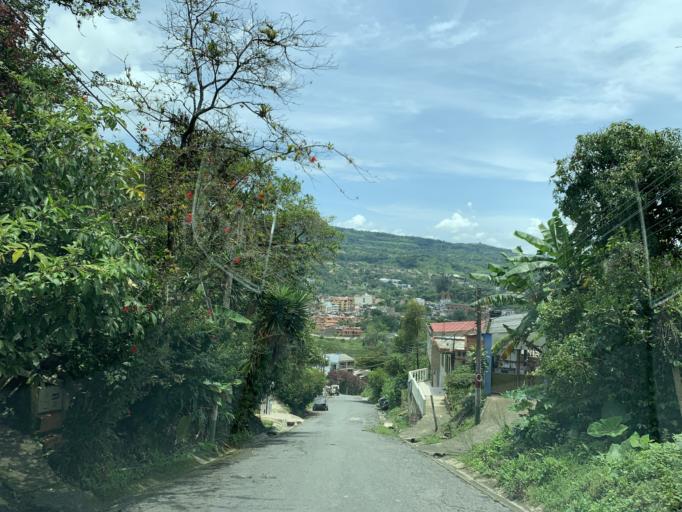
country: CO
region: Boyaca
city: Moniquira
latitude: 5.8747
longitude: -73.5664
